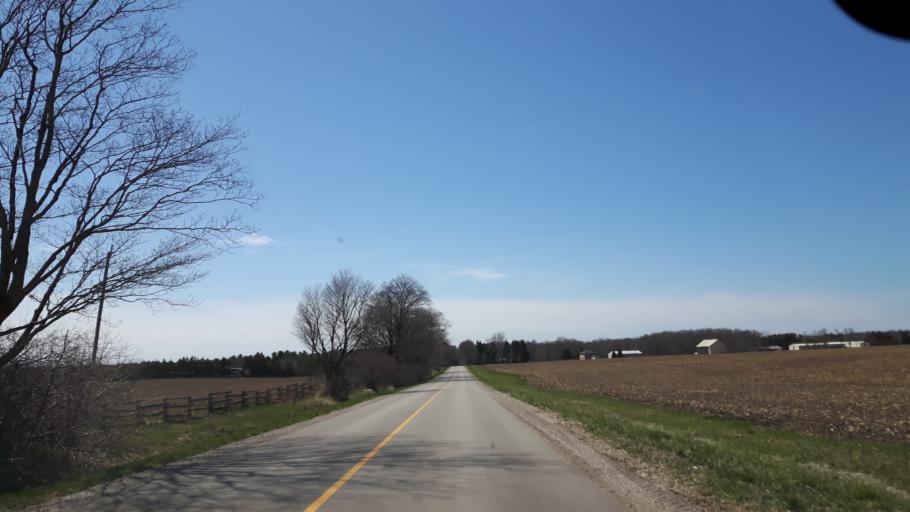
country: CA
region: Ontario
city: Bluewater
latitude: 43.5808
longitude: -81.6572
